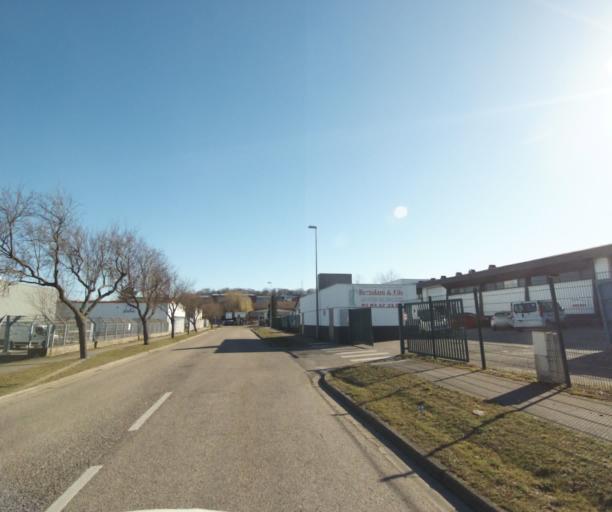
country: FR
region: Lorraine
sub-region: Departement de Meurthe-et-Moselle
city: Vandoeuvre-les-Nancy
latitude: 48.6422
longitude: 6.1875
